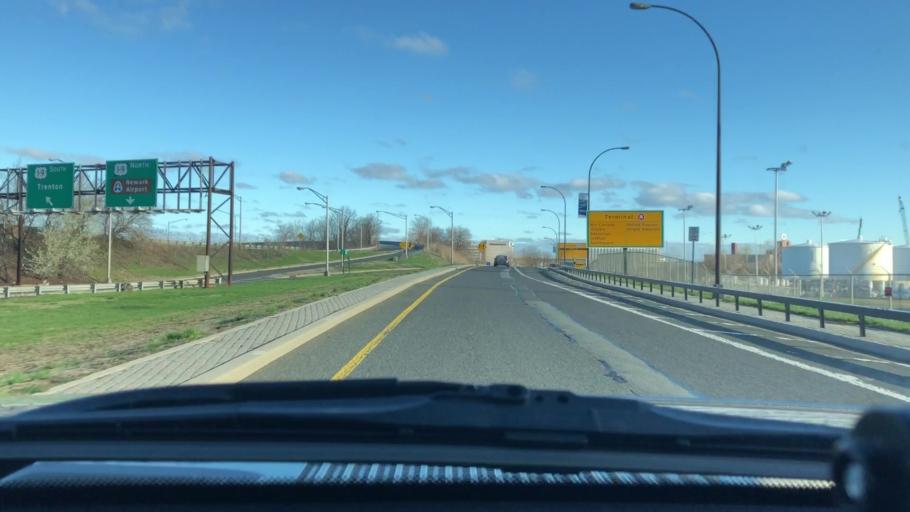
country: US
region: New Jersey
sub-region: Union County
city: Elizabeth
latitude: 40.6773
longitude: -74.1909
